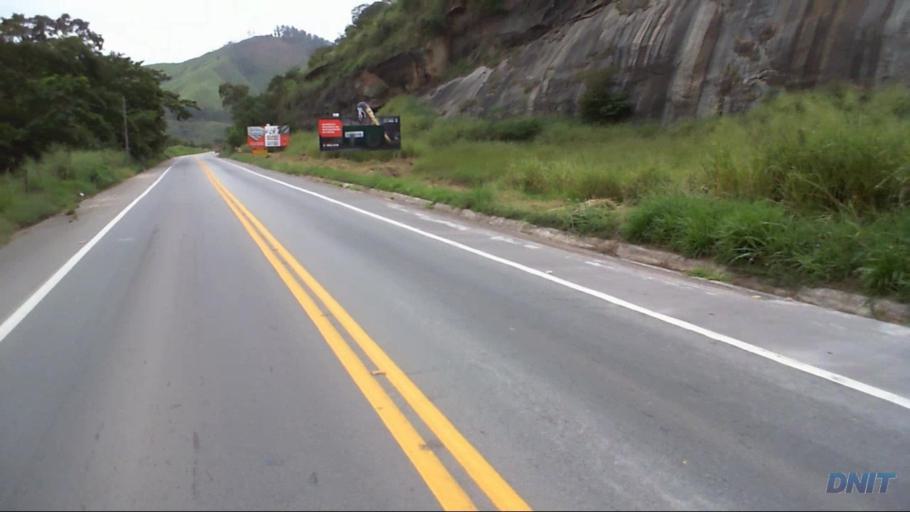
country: BR
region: Minas Gerais
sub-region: Timoteo
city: Timoteo
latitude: -19.5457
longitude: -42.6919
